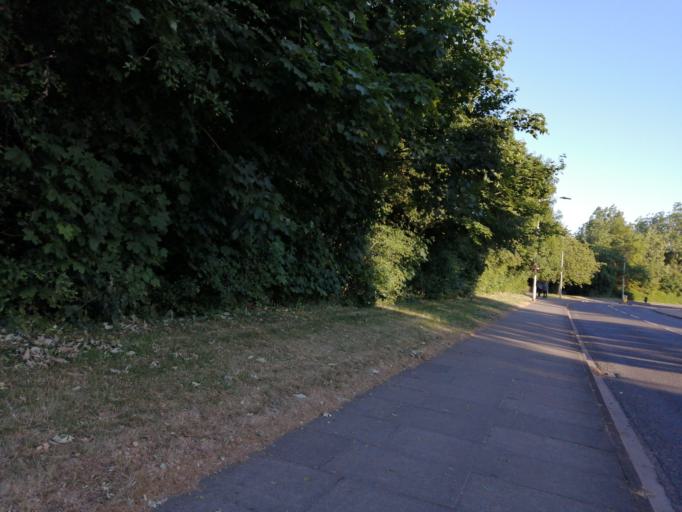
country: GB
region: England
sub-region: Peterborough
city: Peterborough
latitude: 52.5889
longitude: -0.2665
